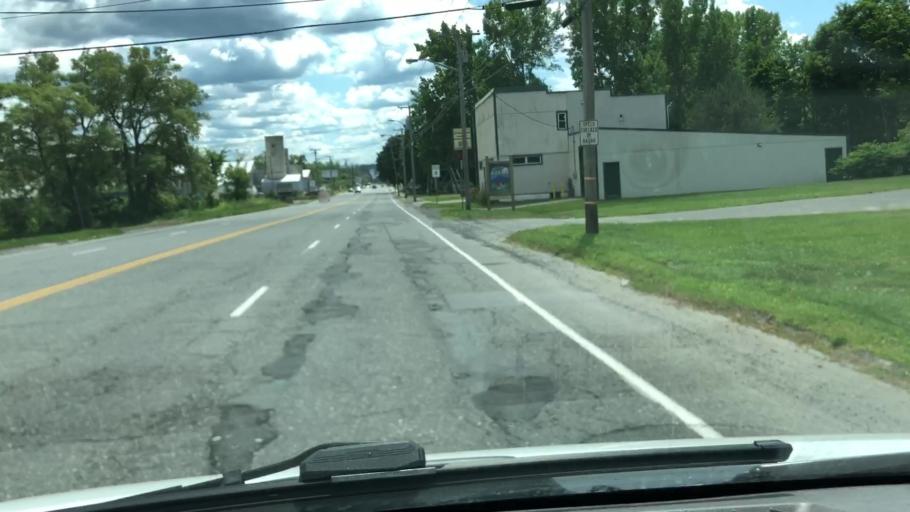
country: US
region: Massachusetts
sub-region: Berkshire County
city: Adams
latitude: 42.6564
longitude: -73.1097
